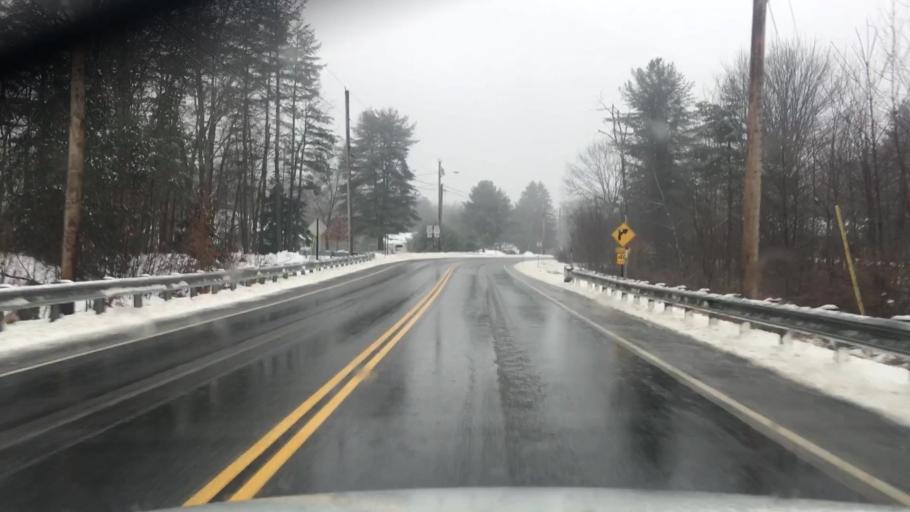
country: US
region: Maine
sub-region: York County
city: Buxton
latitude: 43.5976
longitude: -70.5332
